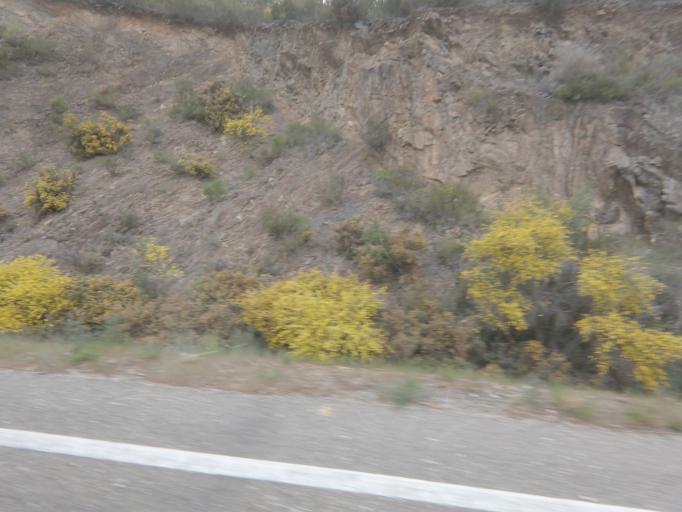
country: ES
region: Extremadura
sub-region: Provincia de Caceres
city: Acebo
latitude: 40.2209
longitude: -6.6756
